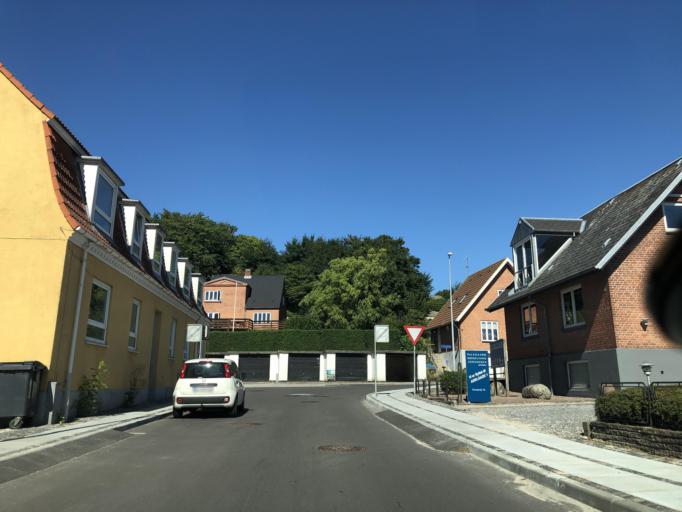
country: DK
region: North Denmark
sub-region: Mariagerfjord Kommune
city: Hobro
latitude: 56.6409
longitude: 9.7991
